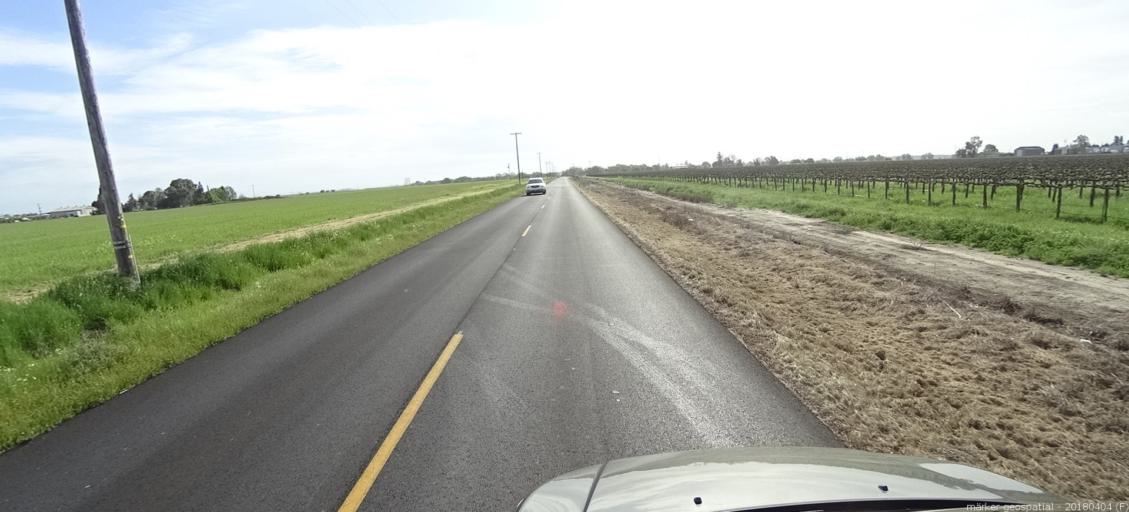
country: US
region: California
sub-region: Sacramento County
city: Herald
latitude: 38.3211
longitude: -121.2319
